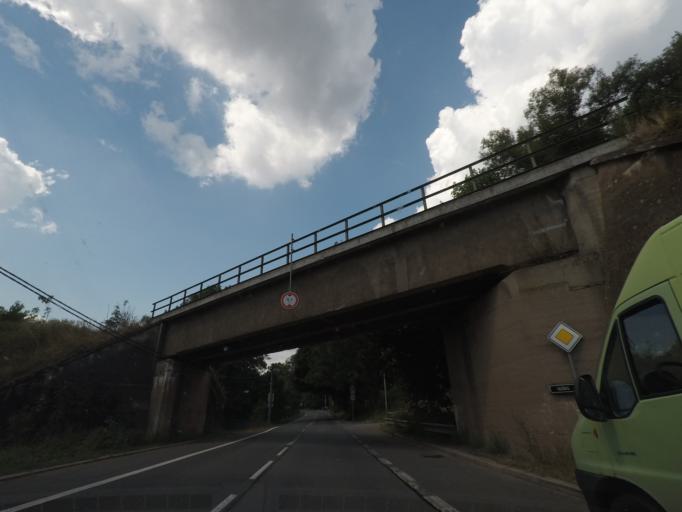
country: CZ
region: Kralovehradecky
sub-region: Okres Trutnov
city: Trutnov
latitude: 50.5586
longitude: 15.8686
